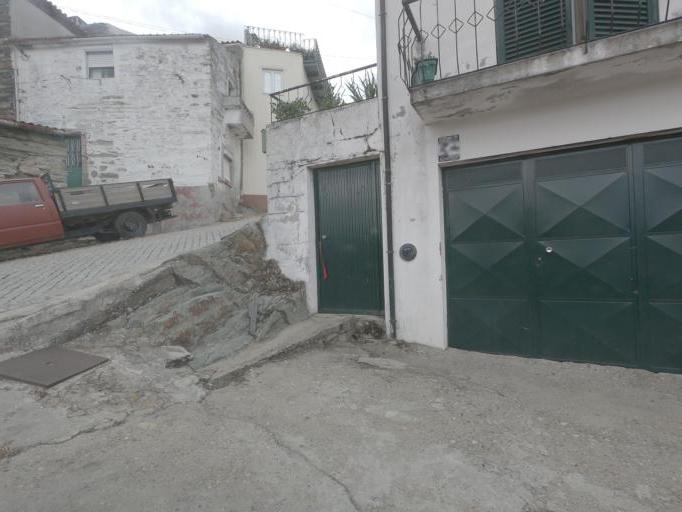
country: PT
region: Vila Real
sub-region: Sabrosa
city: Vilela
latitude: 41.2006
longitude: -7.5346
